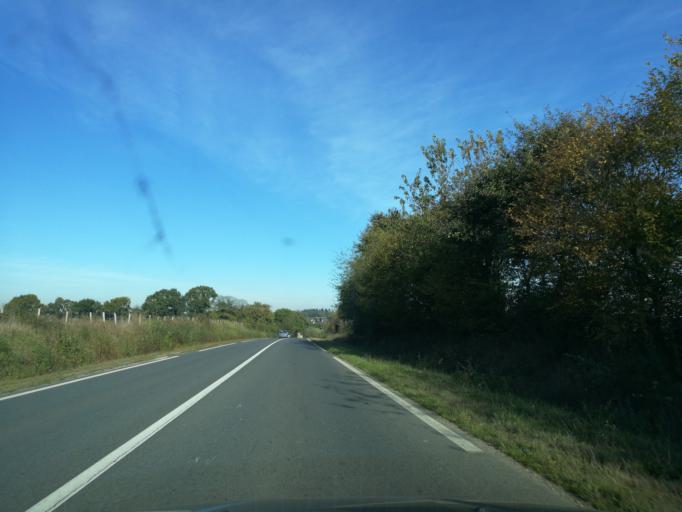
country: FR
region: Brittany
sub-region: Departement d'Ille-et-Vilaine
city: Bedee
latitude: 48.1609
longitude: -1.9453
